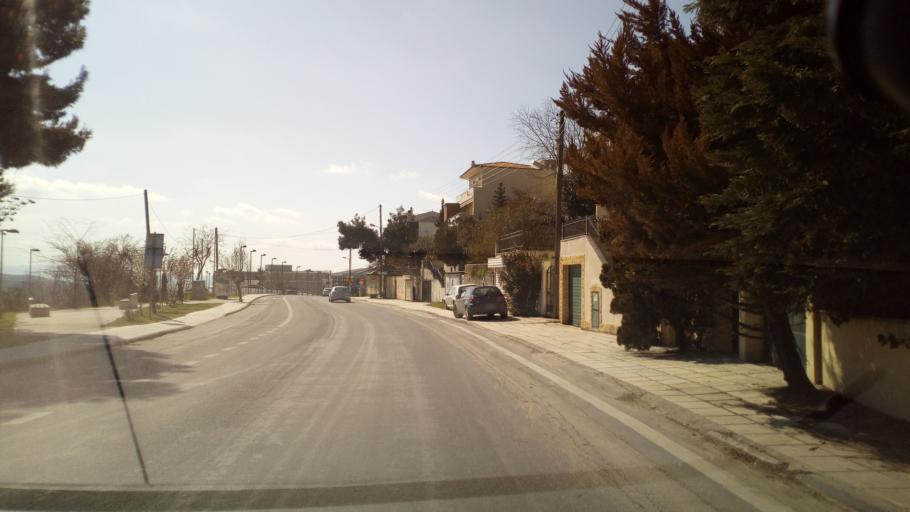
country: GR
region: Central Macedonia
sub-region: Nomos Thessalonikis
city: Panorama
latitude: 40.5876
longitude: 23.0353
